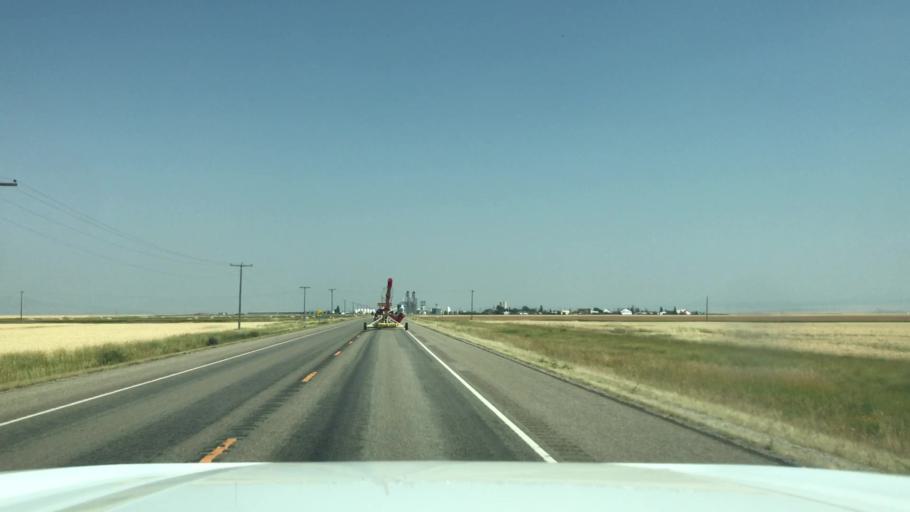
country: US
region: Montana
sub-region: Judith Basin County
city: Stanford
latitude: 47.0552
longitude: -109.9291
